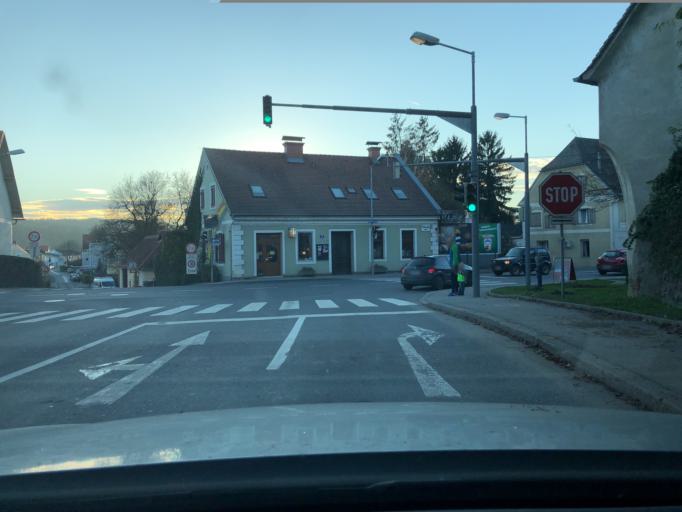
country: AT
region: Styria
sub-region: Politischer Bezirk Weiz
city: Gleisdorf
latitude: 47.1019
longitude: 15.7154
